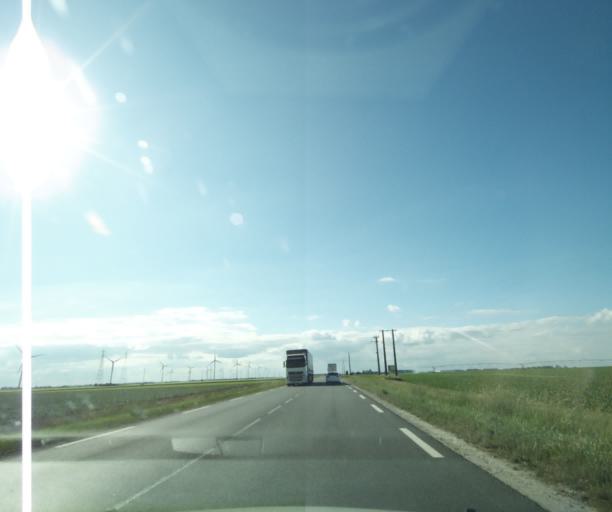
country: FR
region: Centre
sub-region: Departement d'Eure-et-Loir
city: Voves
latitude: 48.3073
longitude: 1.6890
